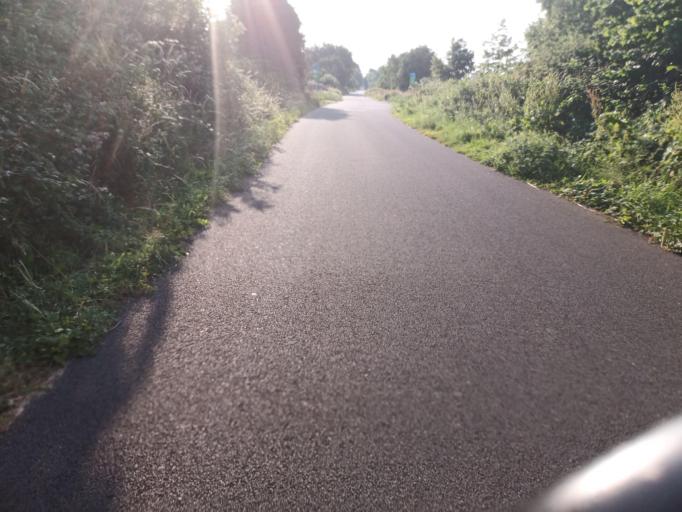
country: GB
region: Northern Ireland
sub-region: Castlereagh District
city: Dundonald
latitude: 54.5905
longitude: -5.8272
